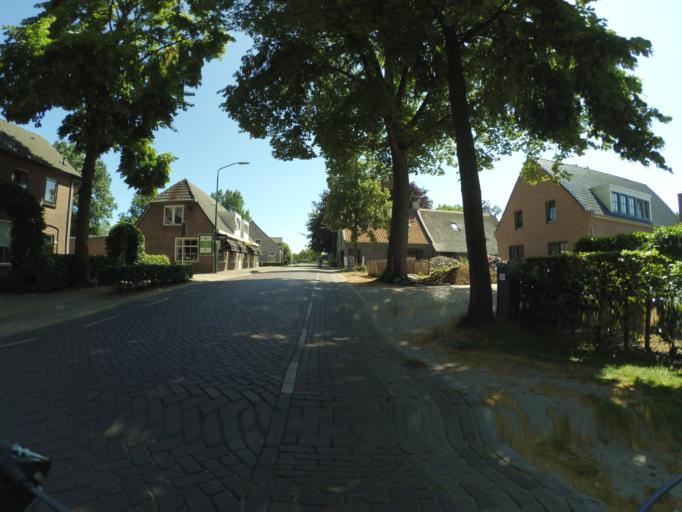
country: NL
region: North Brabant
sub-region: Gemeente Dongen
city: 's Gravenmoer
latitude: 51.6503
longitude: 4.9419
